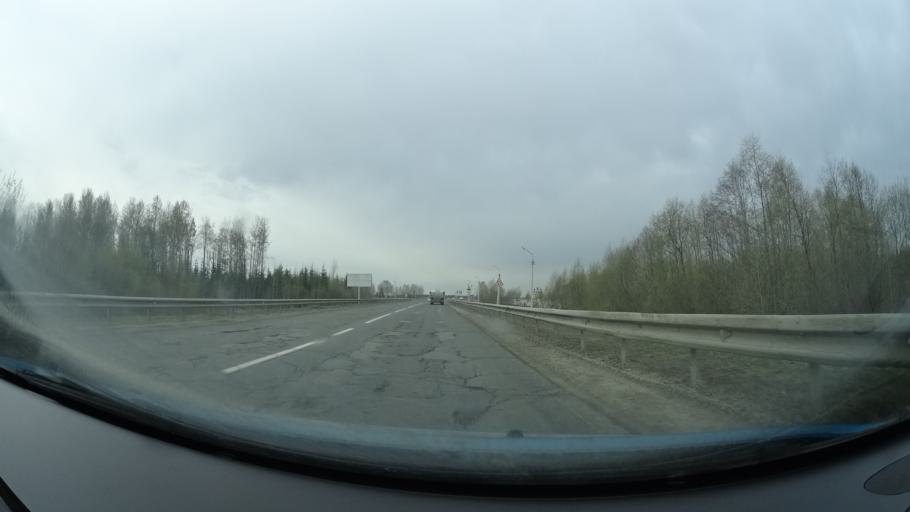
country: RU
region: Perm
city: Ust'-Kachka
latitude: 58.0798
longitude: 55.6605
